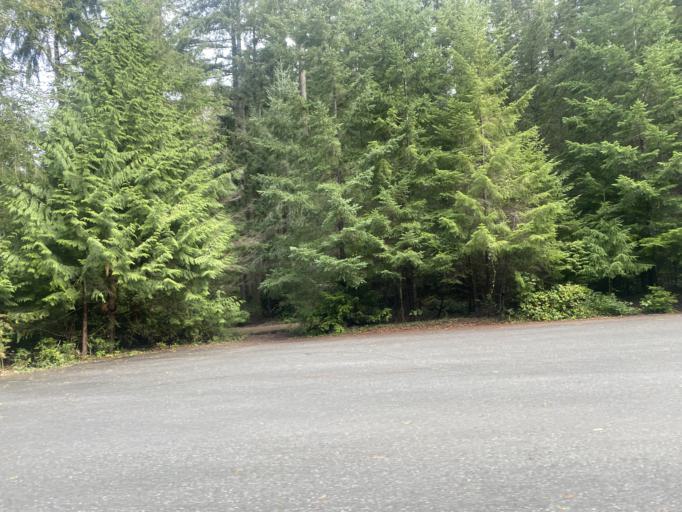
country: US
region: Washington
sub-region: Island County
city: Langley
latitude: 48.0094
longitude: -122.4044
